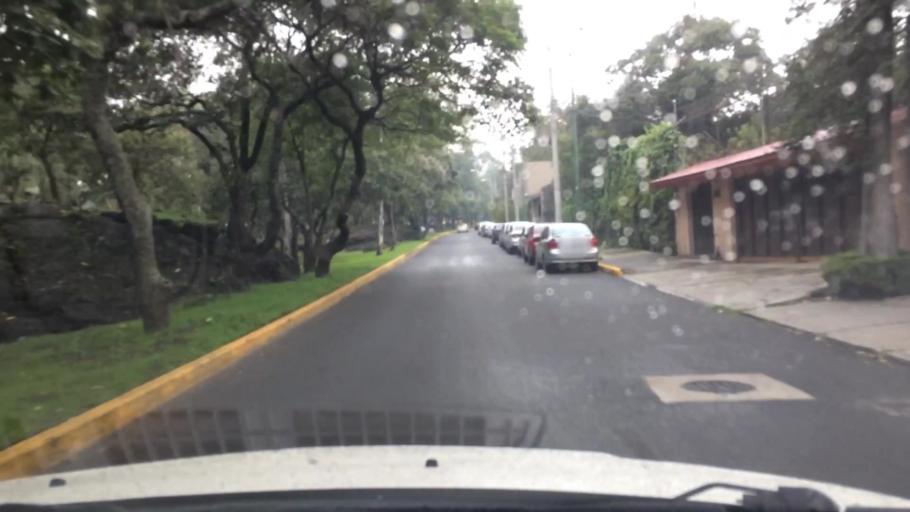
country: MX
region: Mexico City
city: Magdalena Contreras
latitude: 19.3082
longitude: -99.2072
